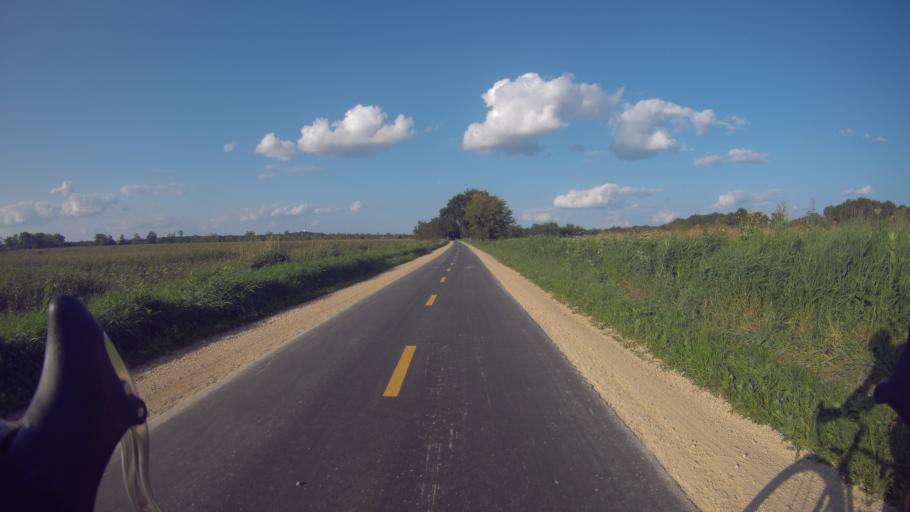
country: US
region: Wisconsin
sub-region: Dane County
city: Monona
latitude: 43.0301
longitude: -89.3333
